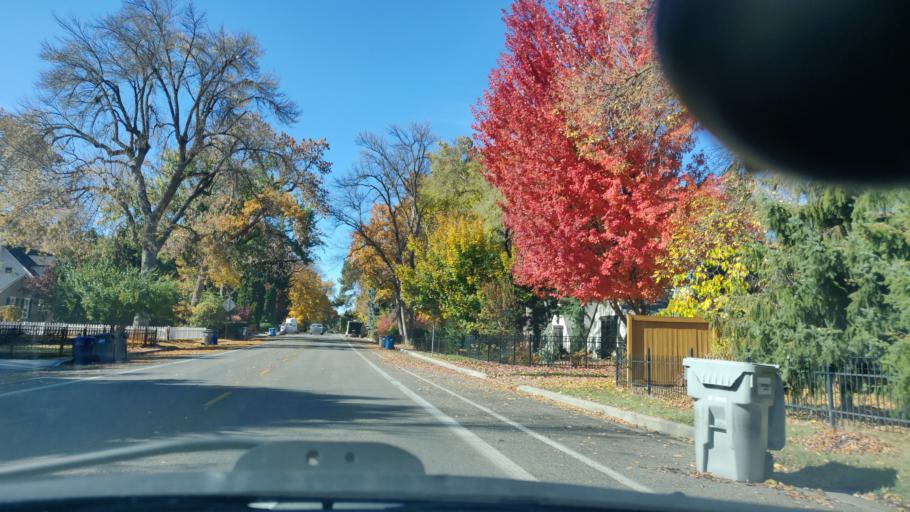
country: US
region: Idaho
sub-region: Ada County
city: Boise
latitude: 43.5935
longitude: -116.2191
